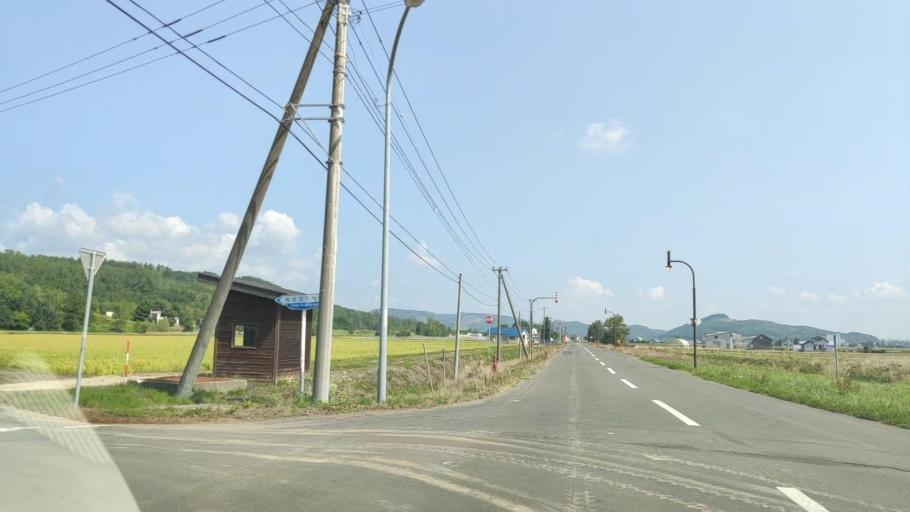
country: JP
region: Hokkaido
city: Shimo-furano
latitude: 43.3763
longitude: 142.3896
